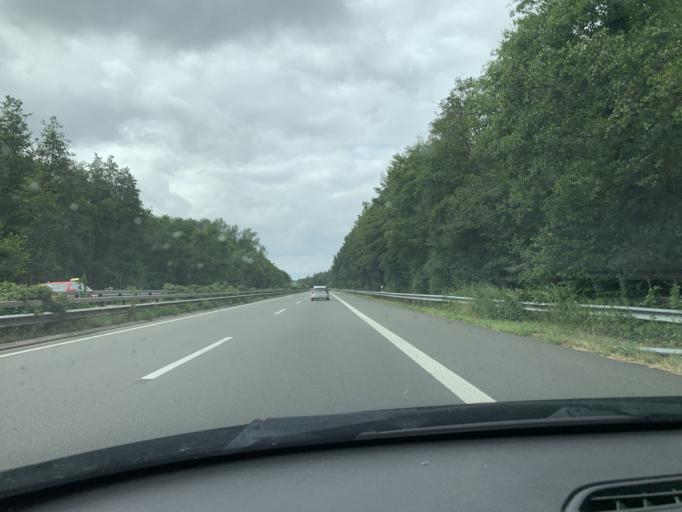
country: DE
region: Lower Saxony
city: Bad Zwischenahn
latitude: 53.2341
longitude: 8.0301
